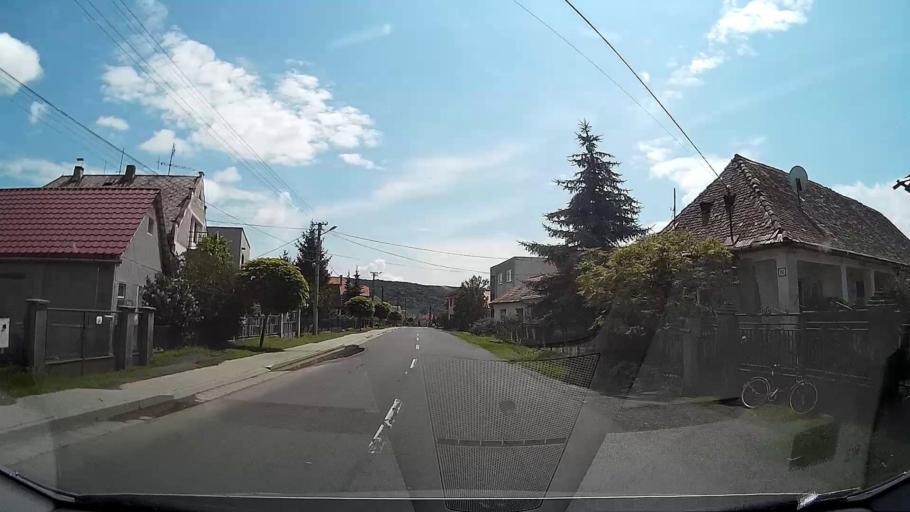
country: SK
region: Banskobystricky
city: Fil'akovo
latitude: 48.3488
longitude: 19.8377
